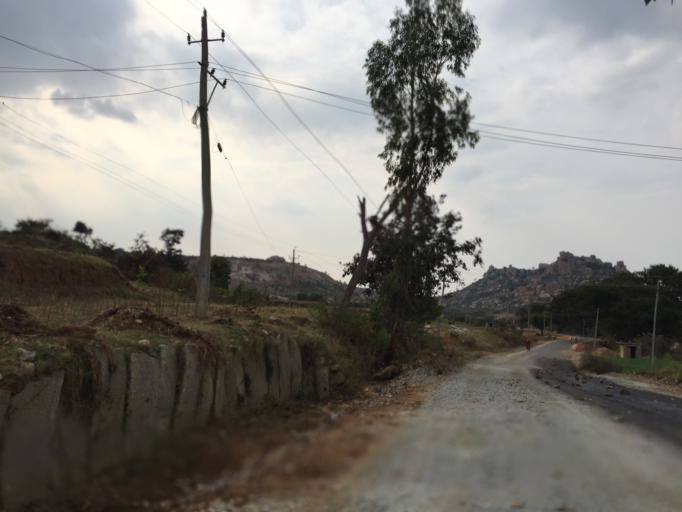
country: IN
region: Karnataka
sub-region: Chikkaballapur
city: Gudibanda
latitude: 13.5564
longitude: 77.7405
